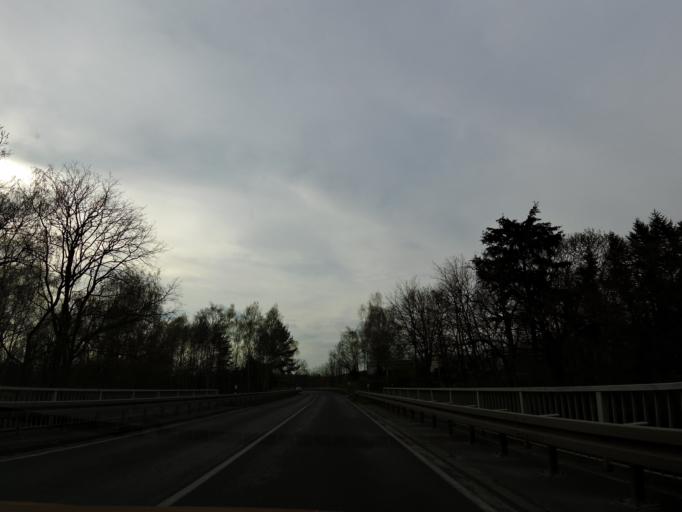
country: DE
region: Brandenburg
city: Mittenwalde
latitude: 52.2582
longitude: 13.5432
